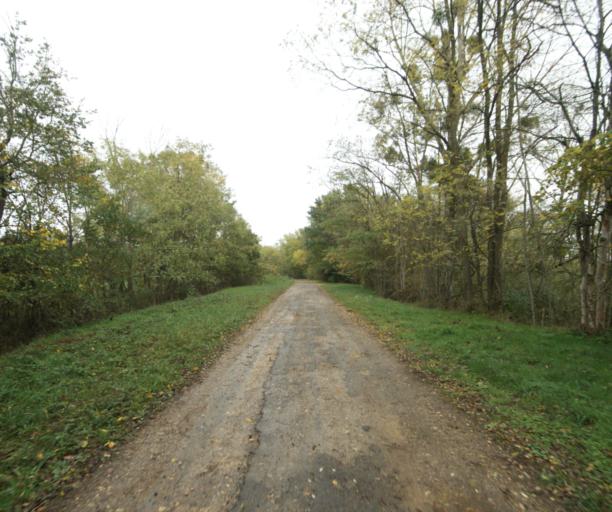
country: FR
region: Rhone-Alpes
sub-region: Departement de l'Ain
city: Pont-de-Vaux
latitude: 46.4589
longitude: 4.8966
